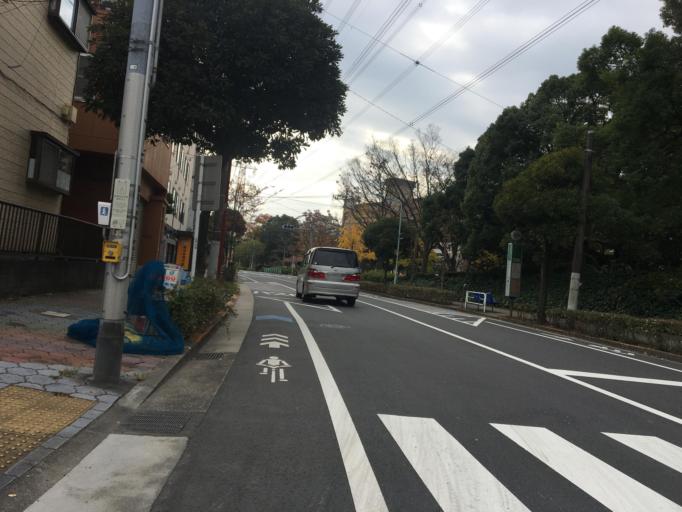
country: JP
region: Tokyo
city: Urayasu
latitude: 35.6591
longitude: 139.8589
